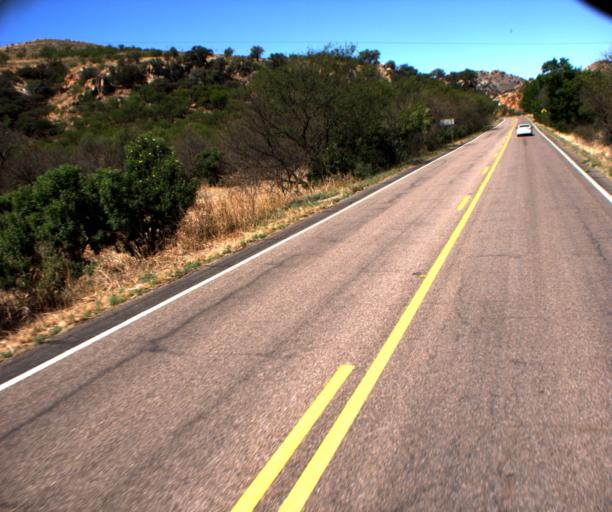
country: US
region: Arizona
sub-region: Santa Cruz County
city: Rio Rico
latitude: 31.5154
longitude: -110.7901
